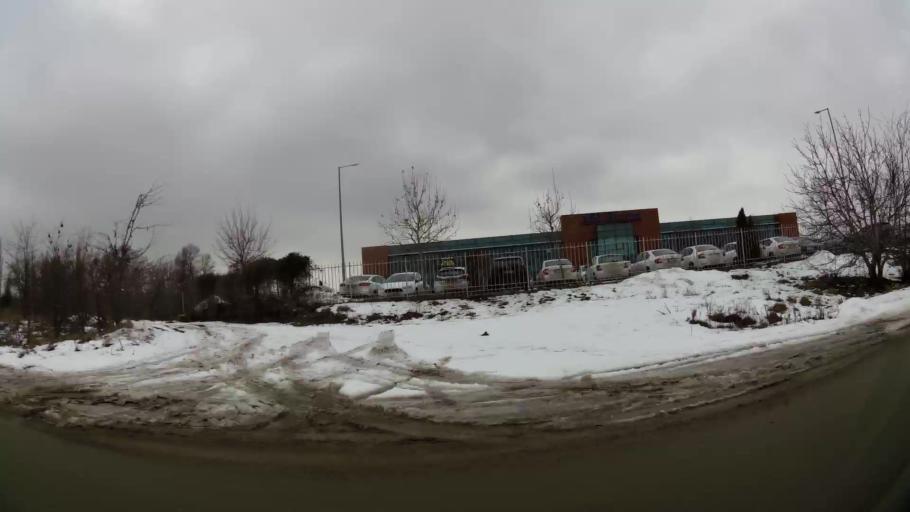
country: RO
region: Ilfov
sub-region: Comuna Chitila
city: Chitila
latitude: 44.5022
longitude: 26.0074
